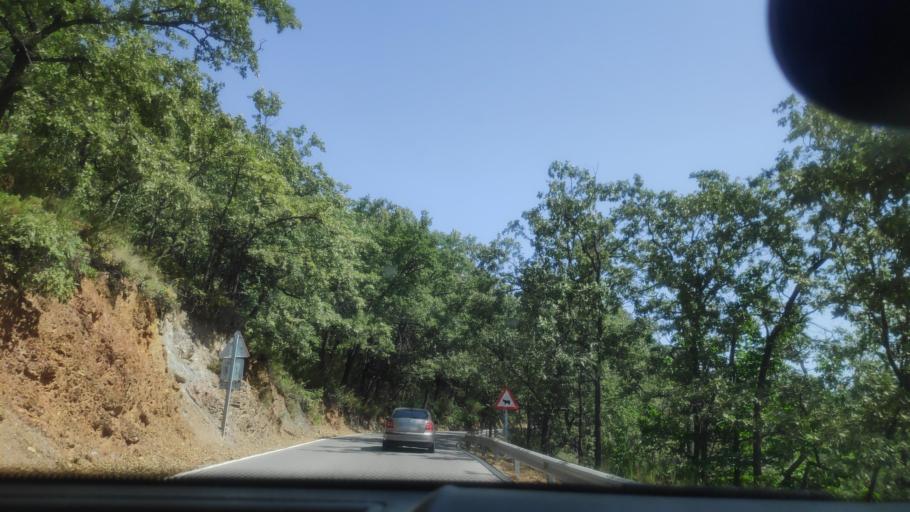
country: ES
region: Andalusia
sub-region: Provincia de Granada
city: Busquistar
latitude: 36.9458
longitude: -3.2852
